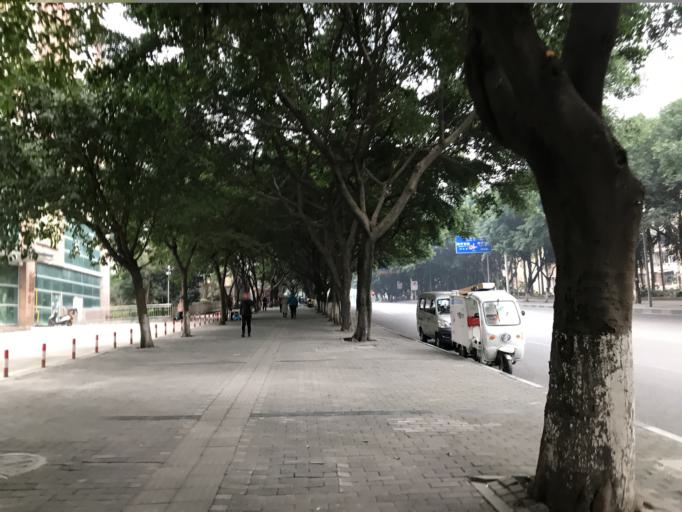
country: CN
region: Chongqing Shi
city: Chongqing
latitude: 29.5295
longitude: 106.5522
